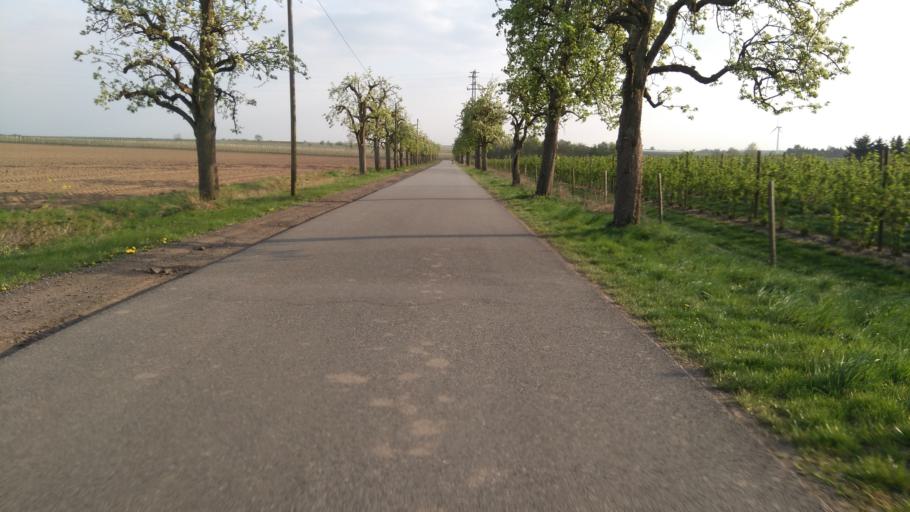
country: DE
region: Lower Saxony
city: Nottensdorf
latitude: 53.4678
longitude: 9.6320
